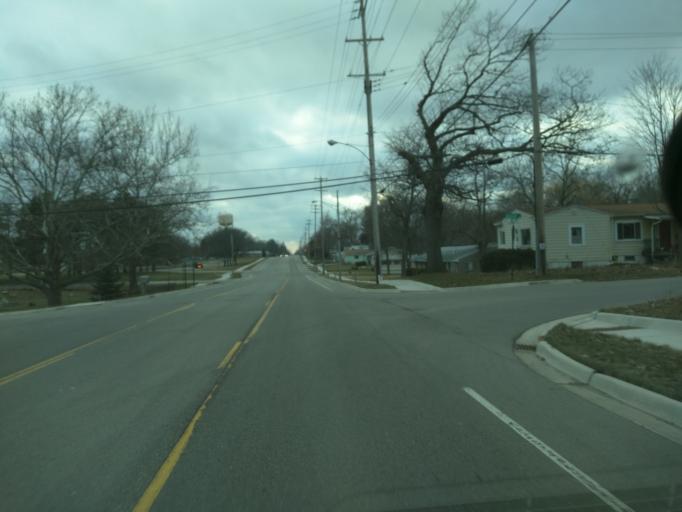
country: US
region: Michigan
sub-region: Ingham County
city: Edgemont Park
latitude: 42.7339
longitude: -84.5885
